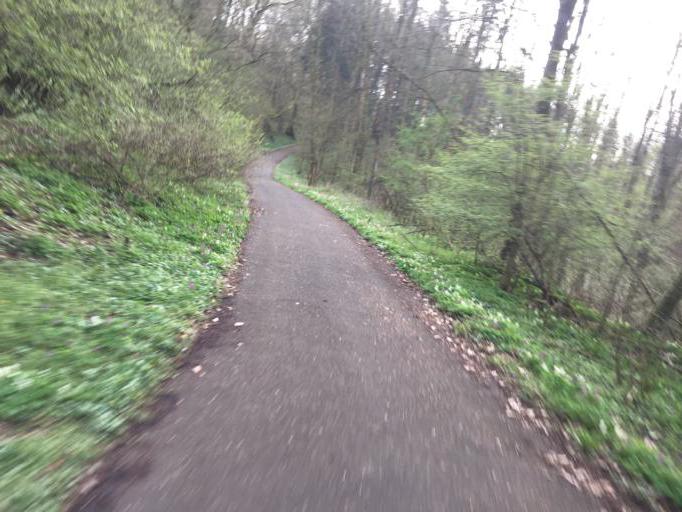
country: DE
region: Hesse
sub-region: Regierungsbezirk Giessen
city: Grunberg
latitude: 50.5878
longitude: 8.9712
